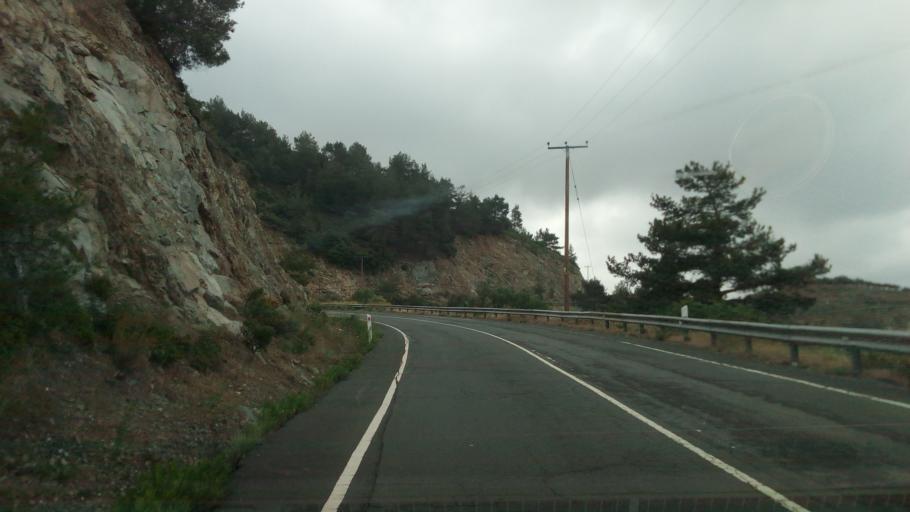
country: CY
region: Limassol
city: Pelendri
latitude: 34.8786
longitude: 32.9960
